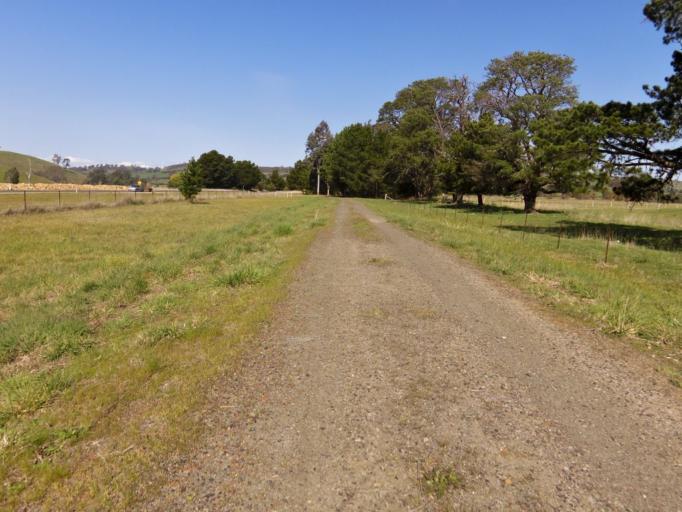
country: AU
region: Victoria
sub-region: Murrindindi
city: Alexandra
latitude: -37.0073
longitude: 145.7511
